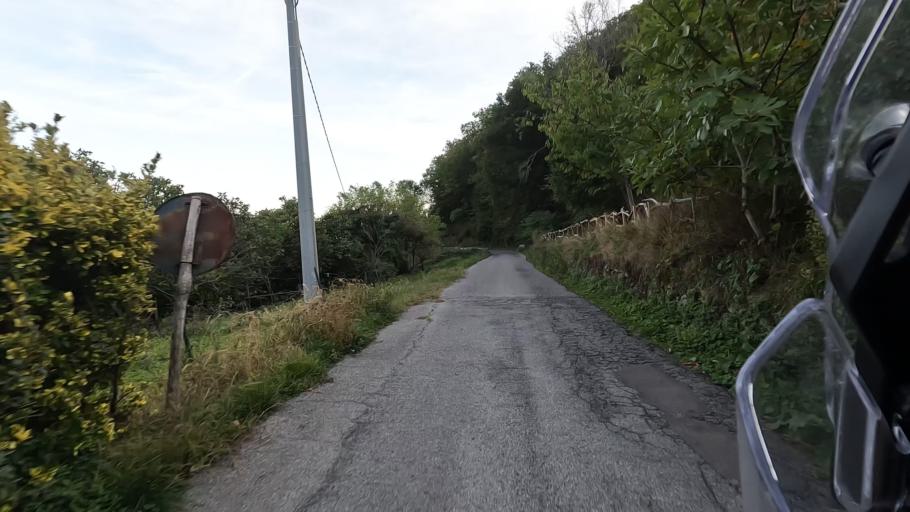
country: IT
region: Liguria
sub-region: Provincia di Savona
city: San Giovanni
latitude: 44.3996
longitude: 8.5331
